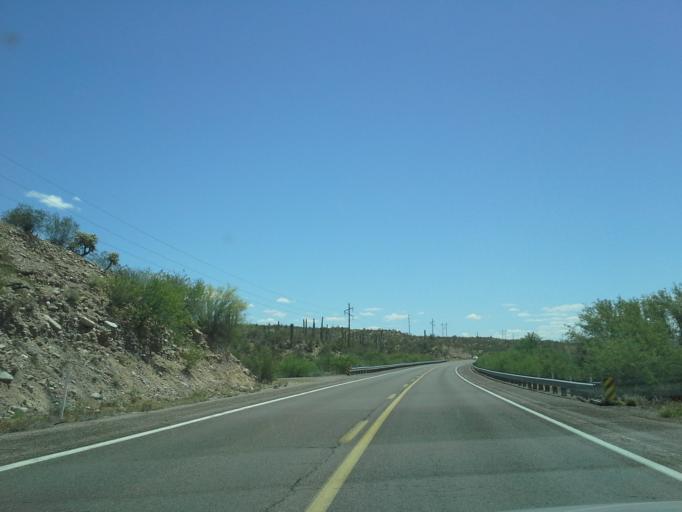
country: US
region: Arizona
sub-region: Pinal County
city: Mammoth
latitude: 32.9148
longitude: -110.7204
